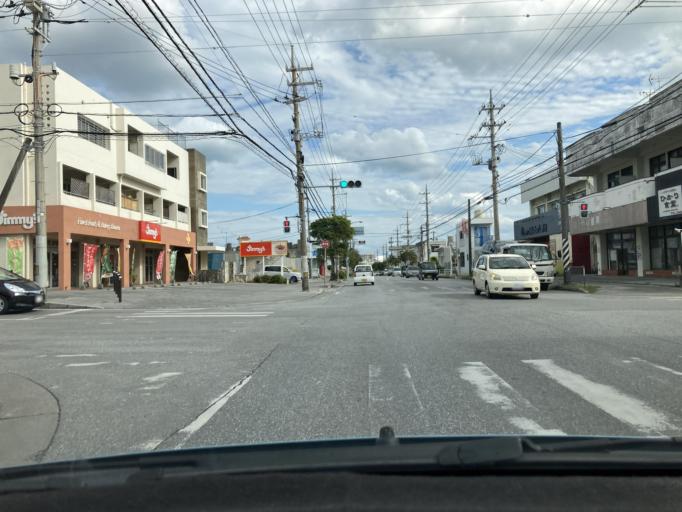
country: JP
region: Okinawa
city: Okinawa
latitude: 26.3585
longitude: 127.8249
